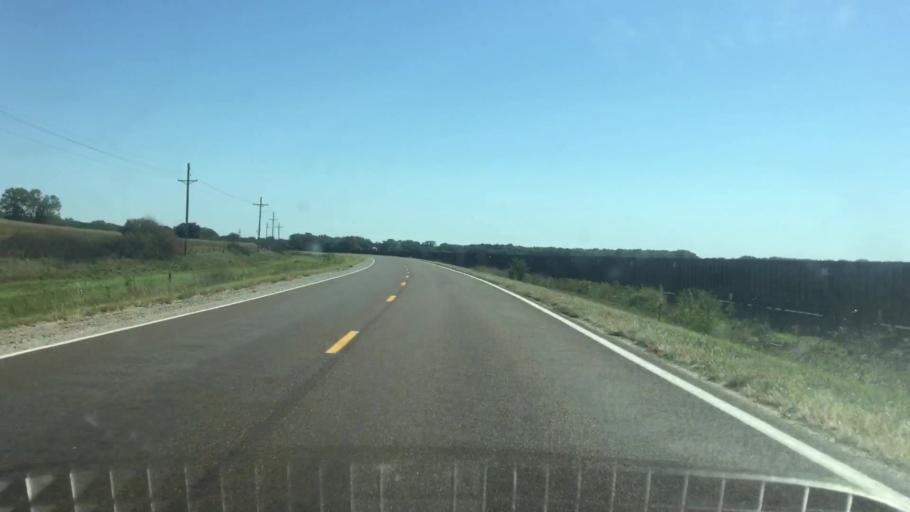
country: US
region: Nebraska
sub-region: Jefferson County
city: Fairbury
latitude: 40.0871
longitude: -97.1186
